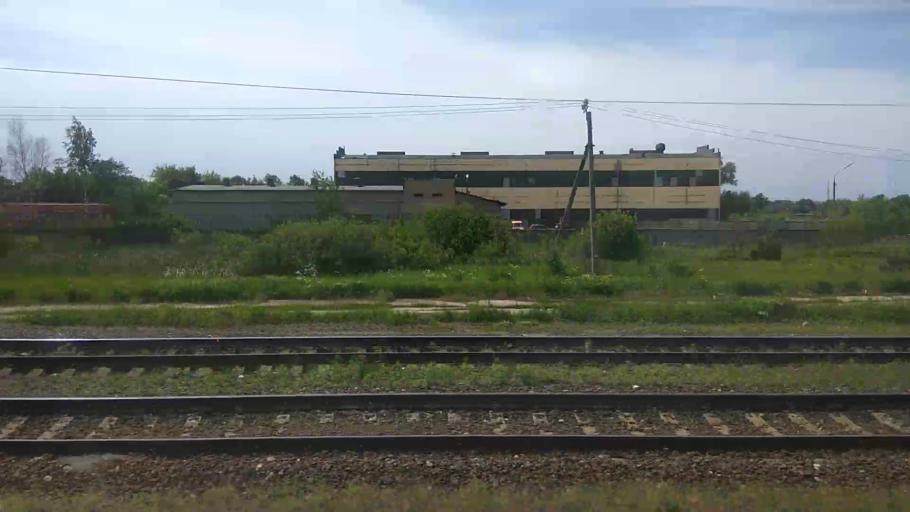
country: RU
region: Moskovskaya
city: Malyshevo
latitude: 55.5029
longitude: 38.3559
